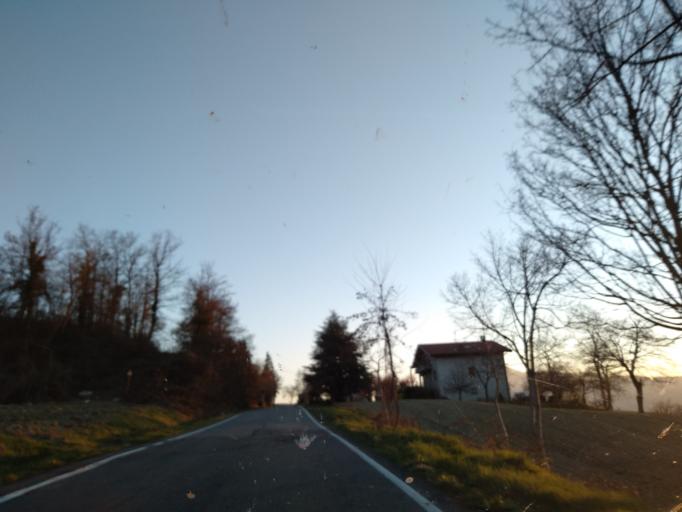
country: IT
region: Emilia-Romagna
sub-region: Provincia di Reggio Emilia
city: Castelnovo ne'Monti
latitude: 44.4263
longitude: 10.4072
